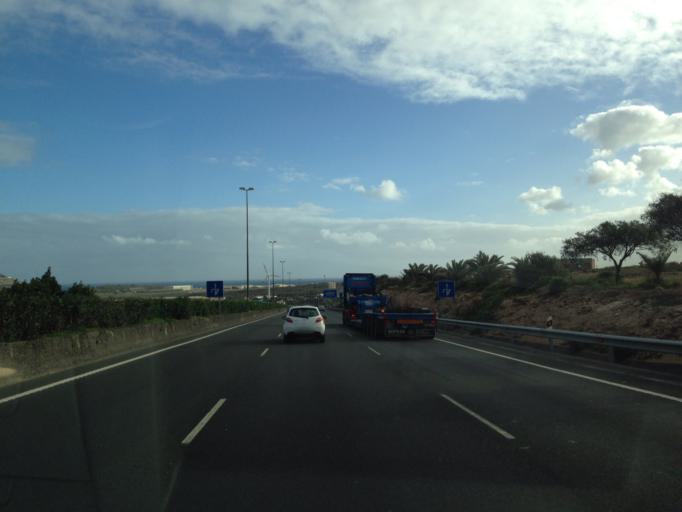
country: ES
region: Canary Islands
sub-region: Provincia de Las Palmas
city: Telde
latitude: 27.9577
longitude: -15.3883
